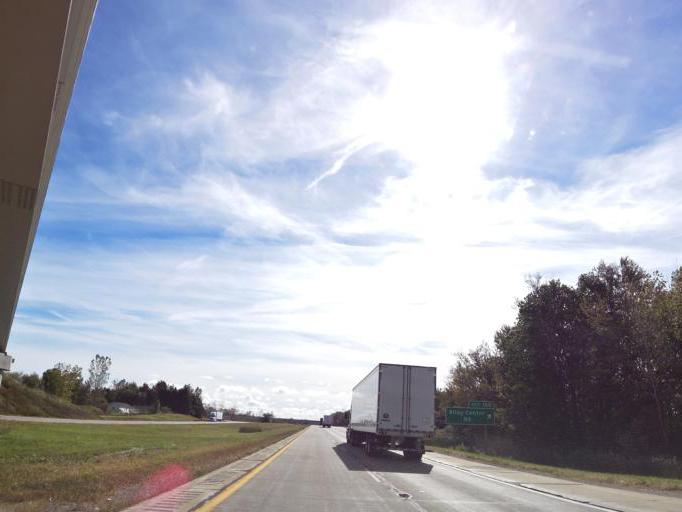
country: US
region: Michigan
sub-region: Saint Clair County
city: Capac
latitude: 42.9843
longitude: -82.8527
